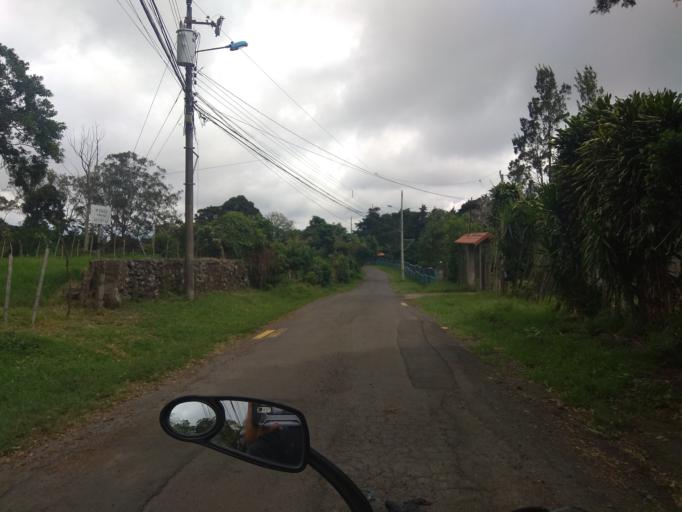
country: CR
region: Heredia
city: San Josecito
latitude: 10.0353
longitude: -84.0972
